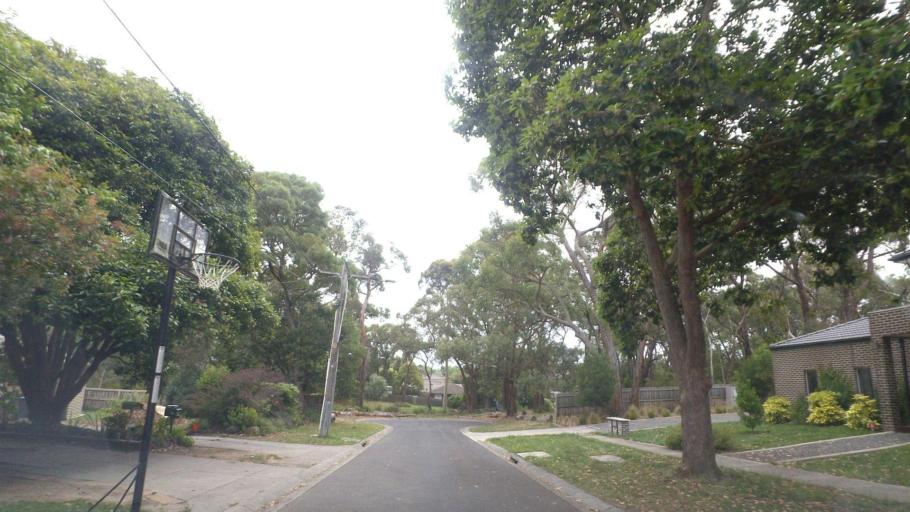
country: AU
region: Victoria
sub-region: Knox
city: The Basin
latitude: -37.8534
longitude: 145.3093
